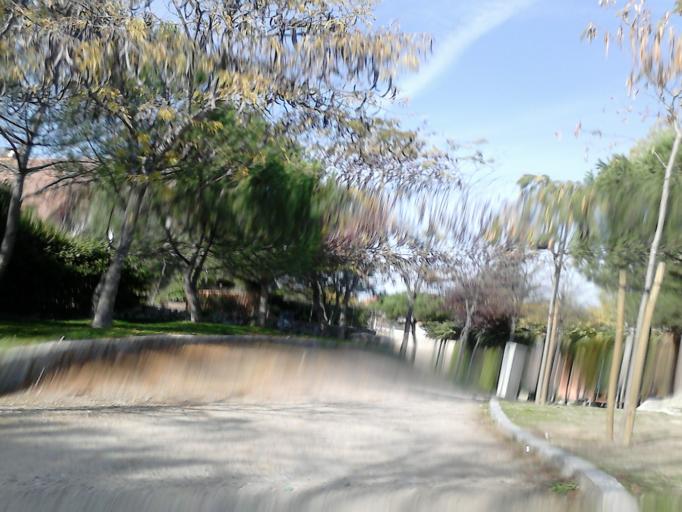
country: ES
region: Madrid
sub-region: Provincia de Madrid
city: Galapagar
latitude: 40.5829
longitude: -4.0065
